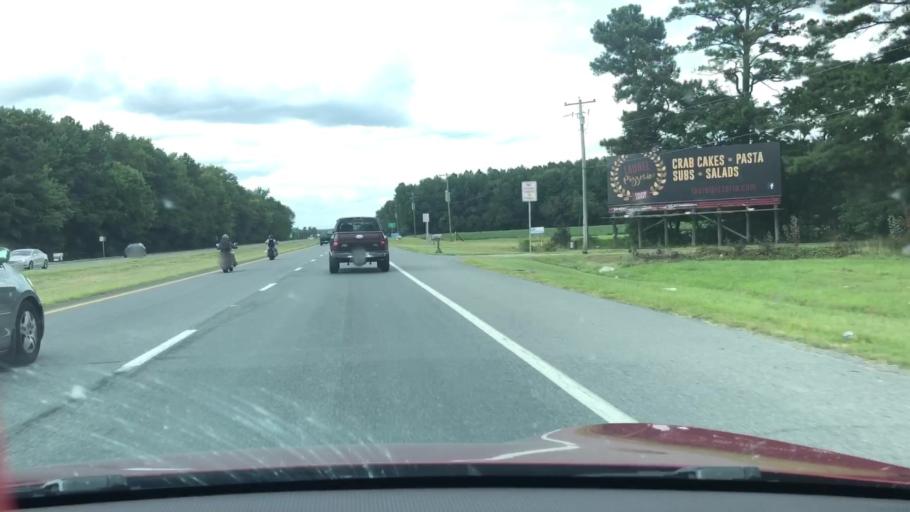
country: US
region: Delaware
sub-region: Sussex County
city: Delmar
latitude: 38.4688
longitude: -75.5601
